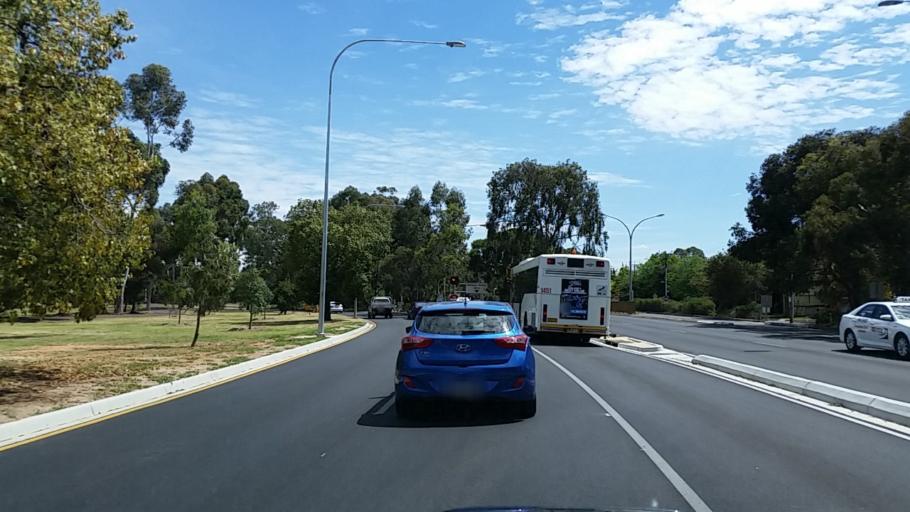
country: AU
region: South Australia
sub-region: Adelaide
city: North Adelaide
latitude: -34.9078
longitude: 138.6127
